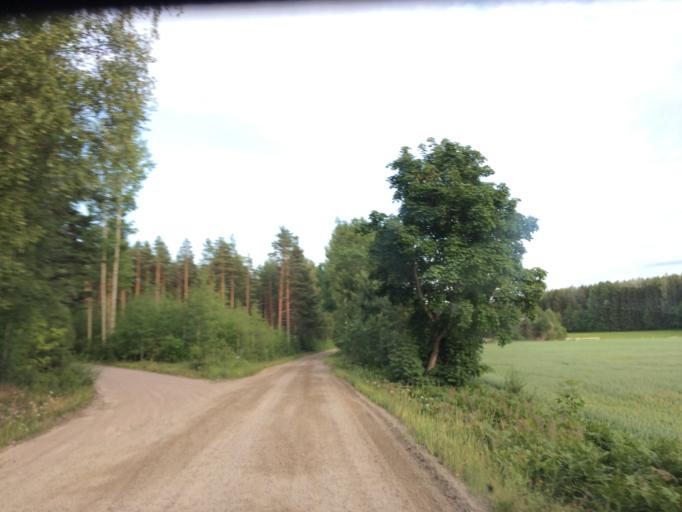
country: FI
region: Haeme
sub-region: Haemeenlinna
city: Janakkala
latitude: 60.8912
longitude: 24.6015
